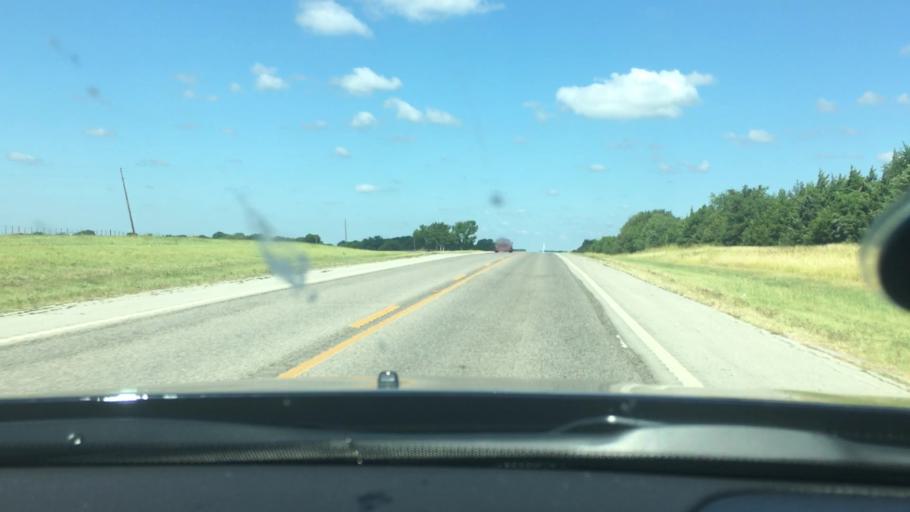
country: US
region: Oklahoma
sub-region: Marshall County
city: Oakland
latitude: 34.1002
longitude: -96.8986
